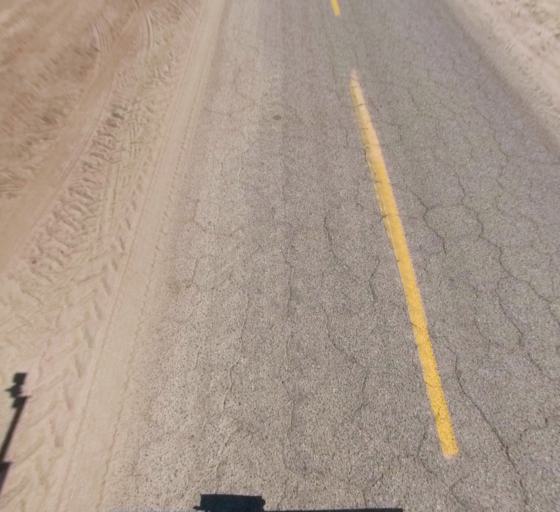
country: US
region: California
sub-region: Fresno County
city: Biola
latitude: 36.8408
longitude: -120.0373
